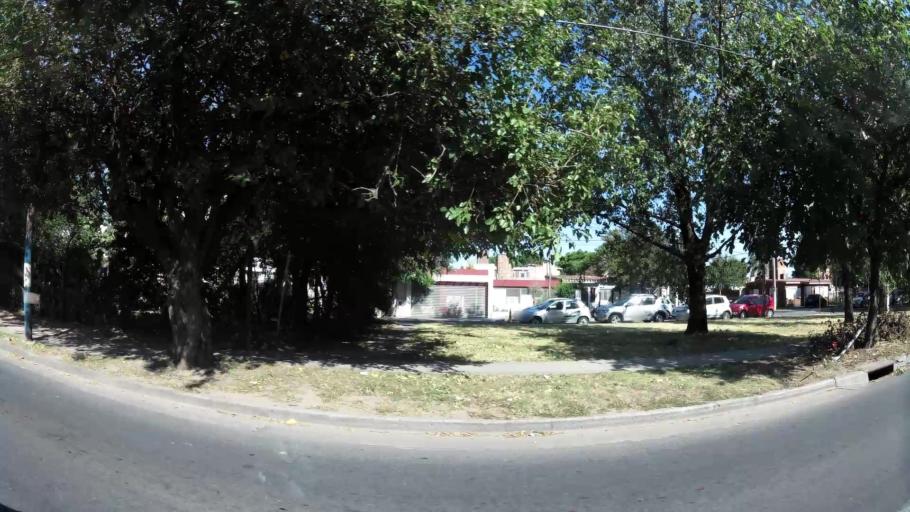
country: AR
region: Cordoba
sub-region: Departamento de Capital
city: Cordoba
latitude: -31.4609
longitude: -64.1868
